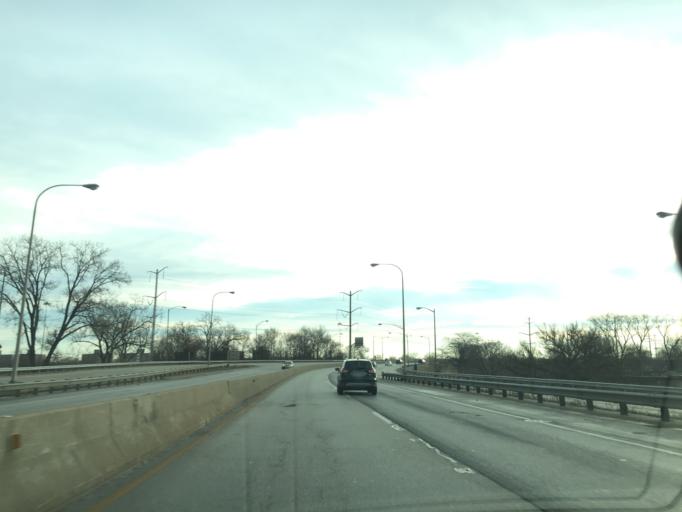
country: US
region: Illinois
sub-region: Cook County
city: Chicago
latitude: 41.7749
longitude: -87.6238
